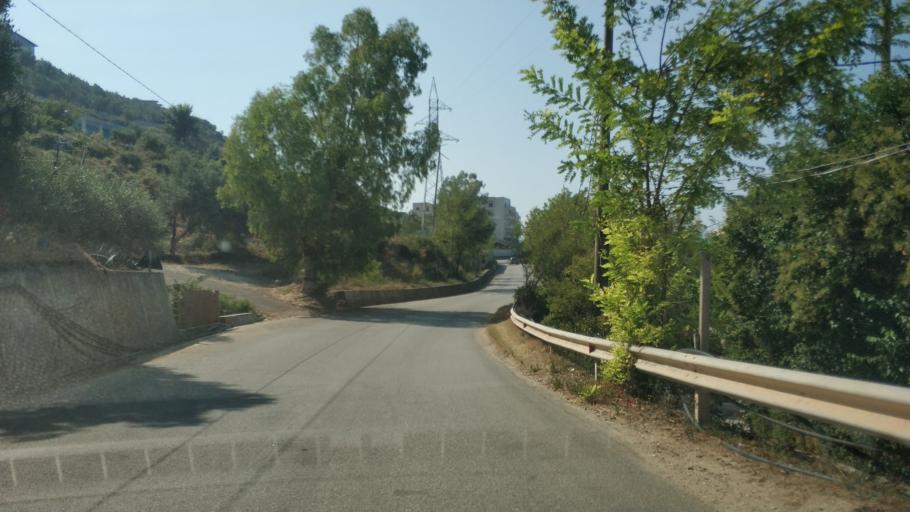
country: AL
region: Vlore
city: Vlore
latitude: 40.4016
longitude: 19.4803
